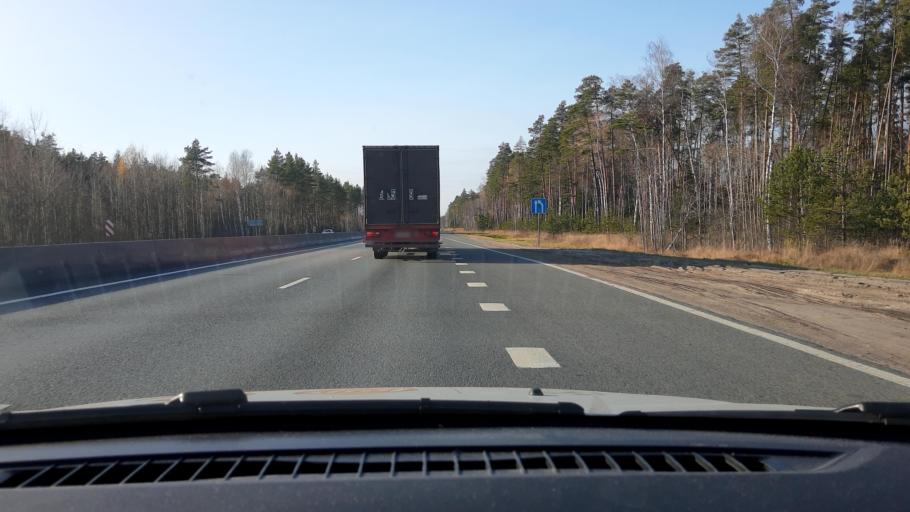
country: RU
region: Nizjnij Novgorod
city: Yuganets
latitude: 56.2896
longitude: 43.2661
